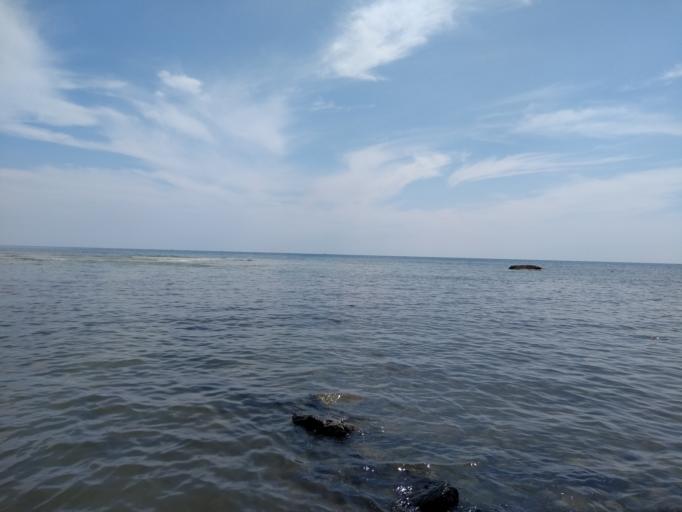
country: TH
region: Trat
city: Ko Chang Tai
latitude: 11.9990
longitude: 102.2960
